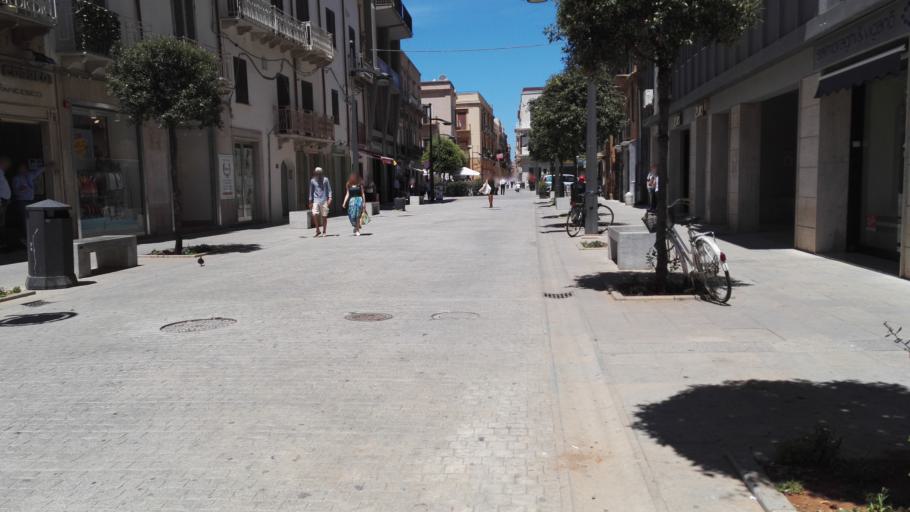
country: IT
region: Sicily
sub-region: Trapani
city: Marsala
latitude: 37.7972
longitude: 12.4379
